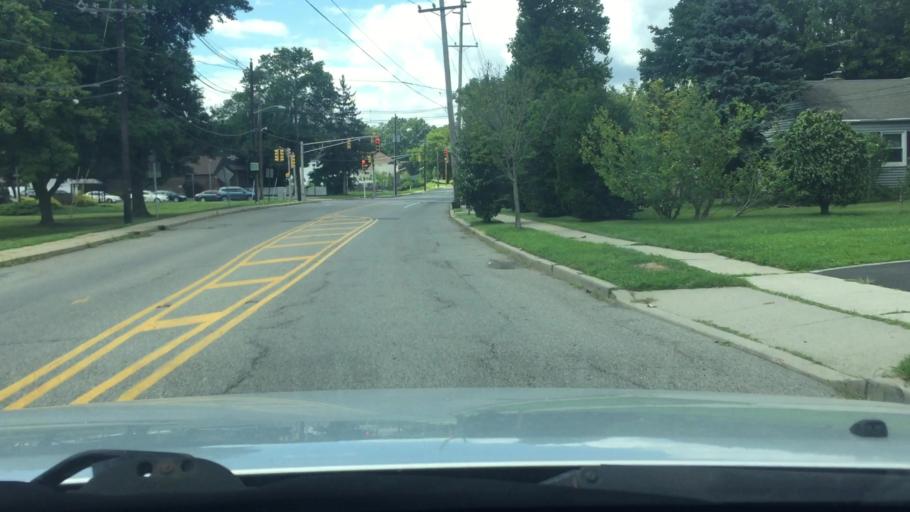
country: US
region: New Jersey
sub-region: Middlesex County
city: East Brunswick
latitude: 40.4244
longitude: -74.4210
